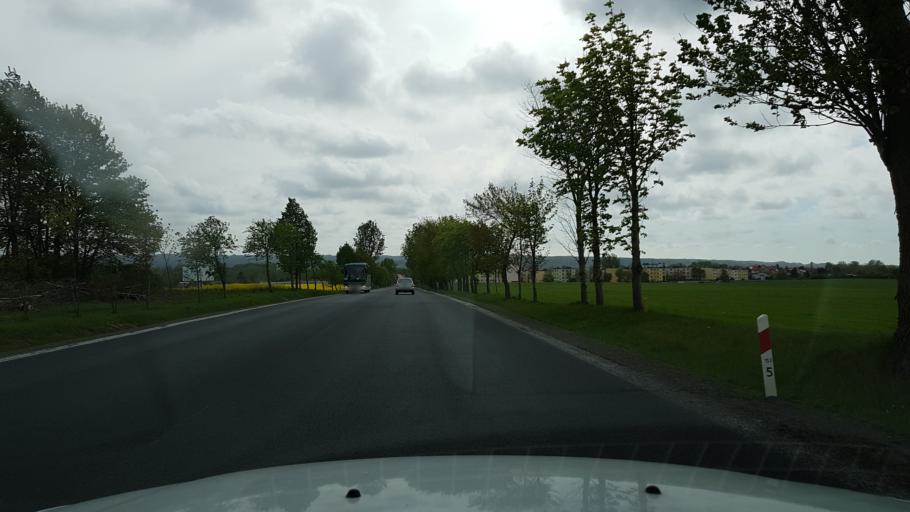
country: PL
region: West Pomeranian Voivodeship
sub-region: Powiat koszalinski
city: Sianow
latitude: 54.2350
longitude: 16.3176
